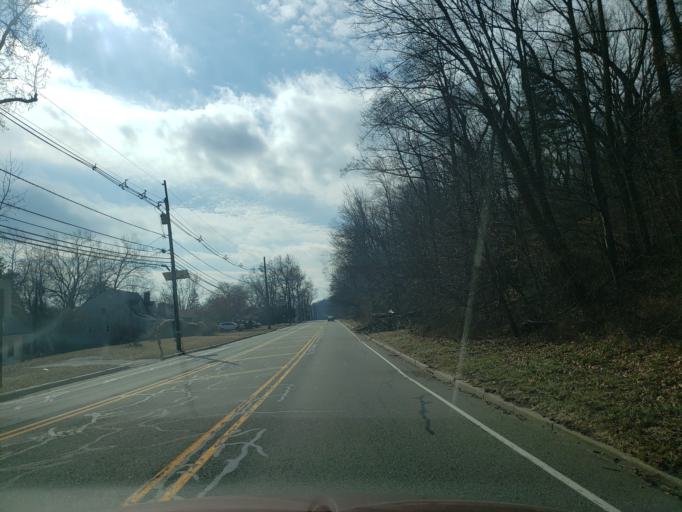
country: US
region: New Jersey
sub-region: Essex County
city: South Orange
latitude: 40.7737
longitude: -74.2832
